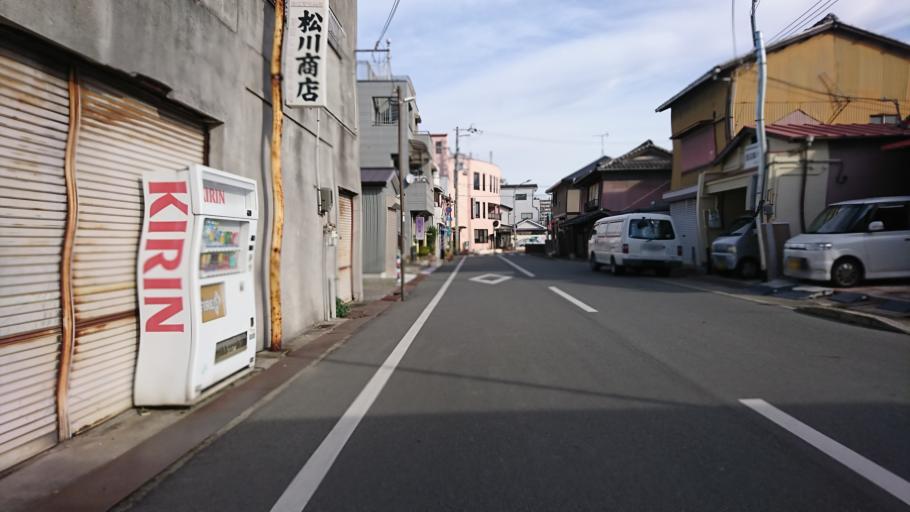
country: JP
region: Hyogo
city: Kakogawacho-honmachi
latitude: 34.7462
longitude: 134.8003
